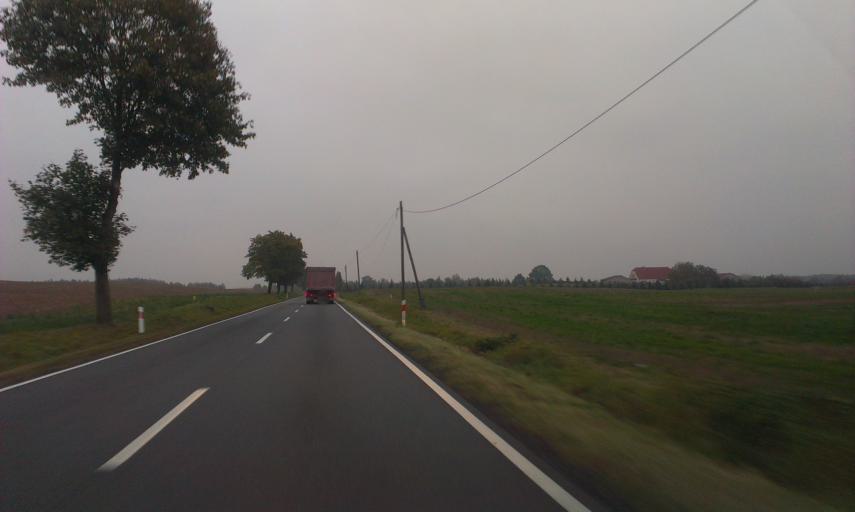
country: PL
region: Kujawsko-Pomorskie
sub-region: Powiat sepolenski
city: Sepolno Krajenskie
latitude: 53.4382
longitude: 17.6146
